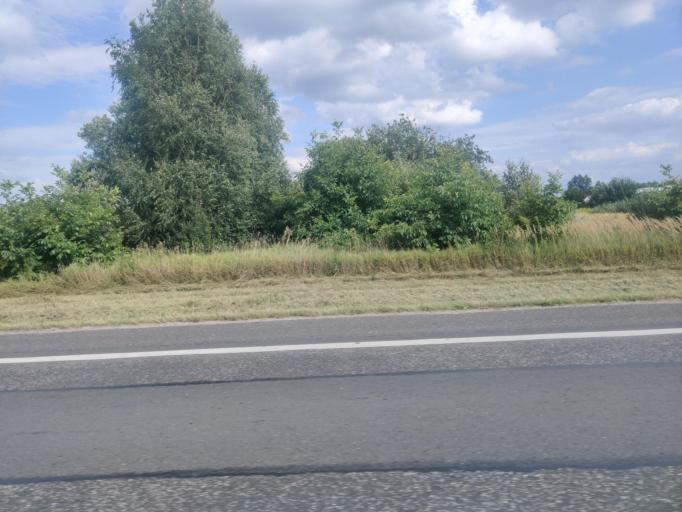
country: PL
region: Greater Poland Voivodeship
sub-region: Konin
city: Konin
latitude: 52.1970
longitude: 18.2683
